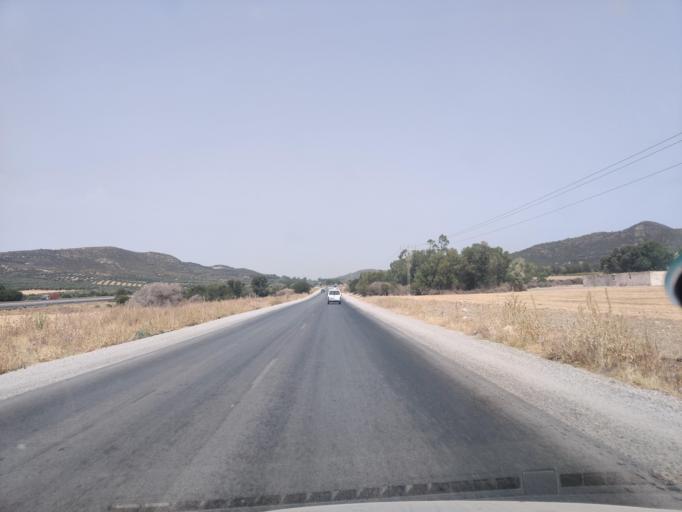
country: TN
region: Tunis
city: Hammam-Lif
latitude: 36.6257
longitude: 10.3999
